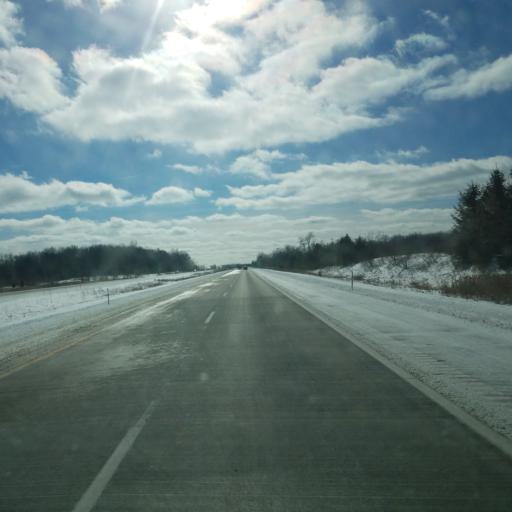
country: US
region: Michigan
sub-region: Clinton County
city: DeWitt
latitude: 42.8404
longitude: -84.5190
